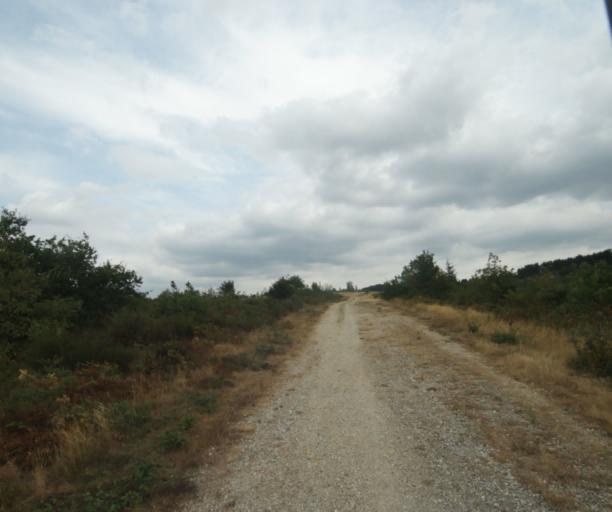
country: FR
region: Midi-Pyrenees
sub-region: Departement de la Haute-Garonne
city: Revel
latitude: 43.4446
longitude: 2.0102
